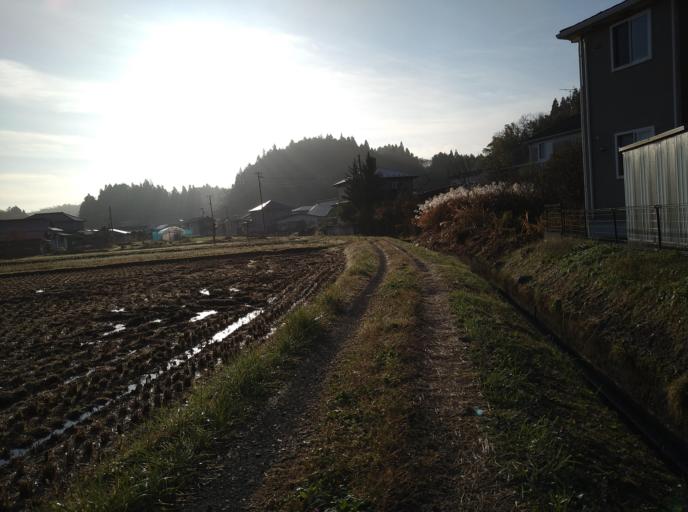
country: JP
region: Iwate
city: Ichinoseki
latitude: 38.9144
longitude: 141.1022
